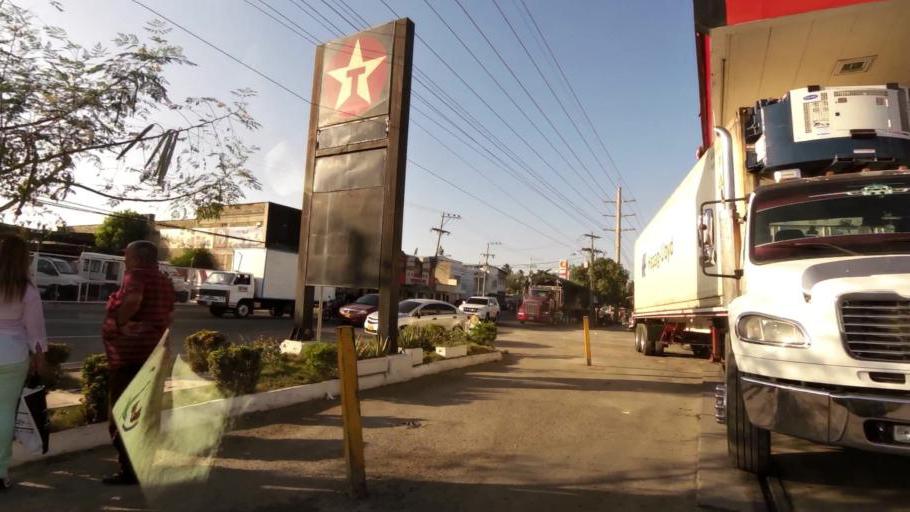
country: CO
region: Bolivar
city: Cartagena
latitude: 10.3985
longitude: -75.5216
